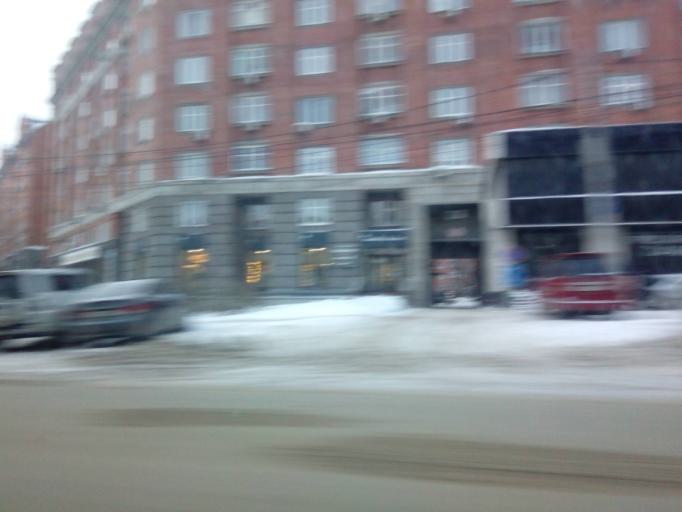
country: RU
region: Novosibirsk
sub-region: Novosibirskiy Rayon
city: Novosibirsk
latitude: 55.0321
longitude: 82.9099
